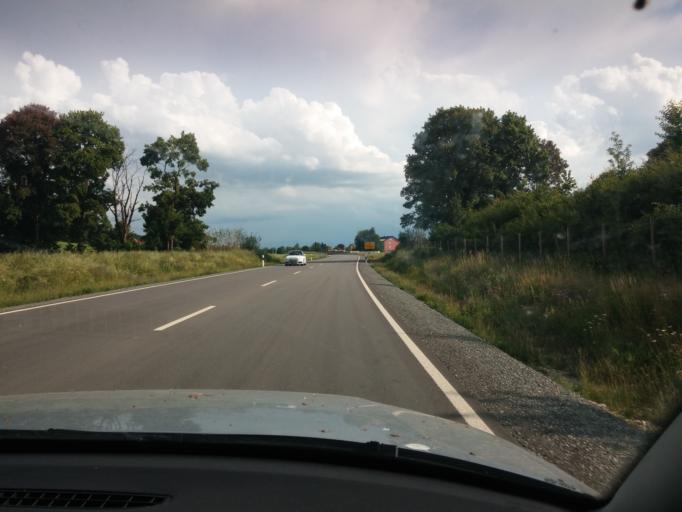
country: DE
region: Bavaria
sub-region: Upper Bavaria
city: Grafing bei Munchen
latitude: 48.0502
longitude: 11.9750
